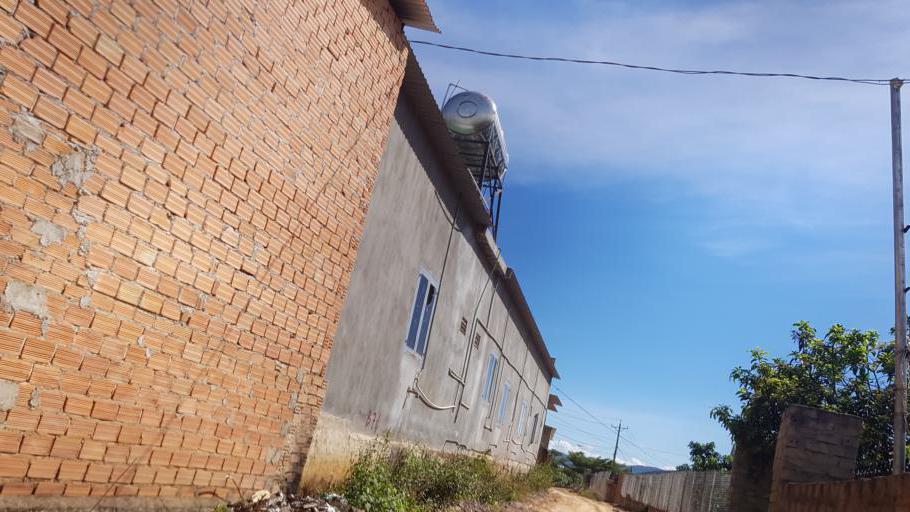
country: VN
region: Lam Dong
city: Da Lat
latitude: 11.8797
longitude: 108.3418
